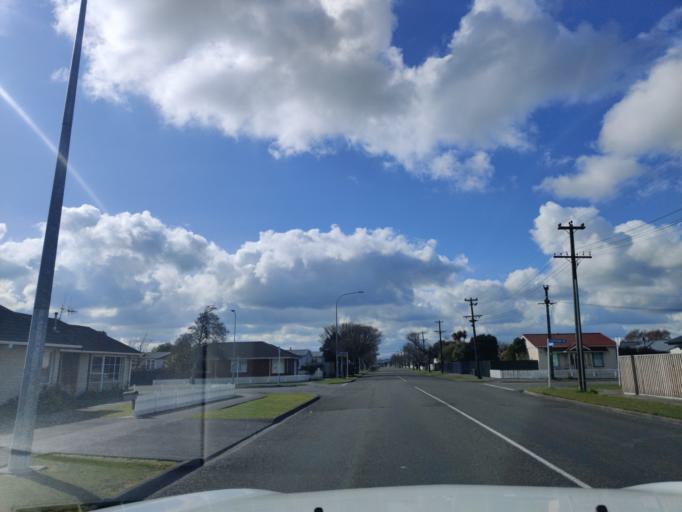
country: NZ
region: Manawatu-Wanganui
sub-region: Palmerston North City
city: Palmerston North
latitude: -40.3338
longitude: 175.6117
